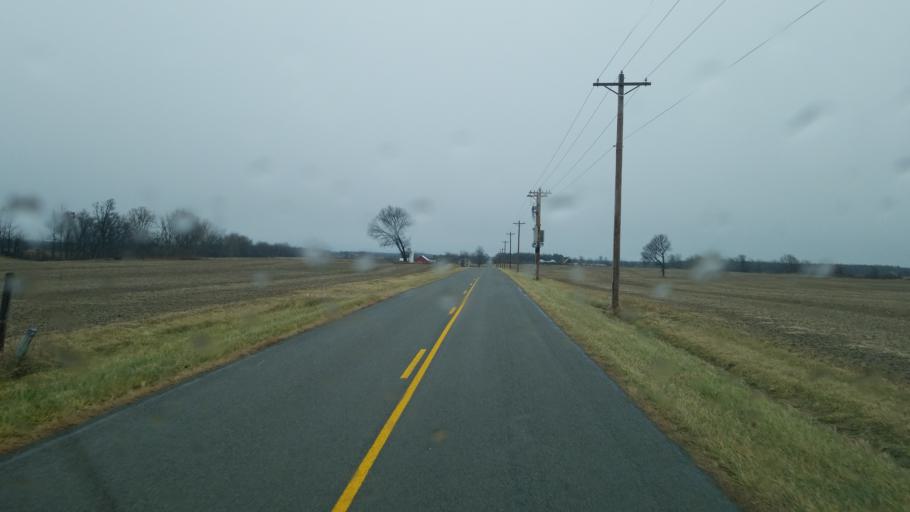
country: US
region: Ohio
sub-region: Logan County
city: Northwood
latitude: 40.4465
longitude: -83.6286
